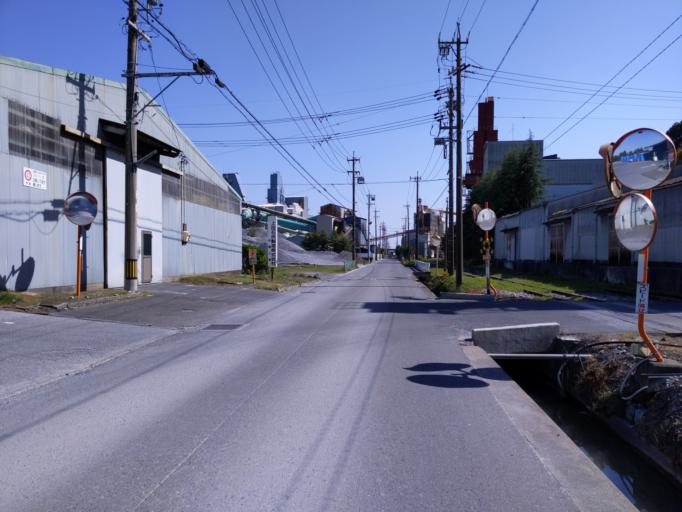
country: JP
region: Gifu
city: Godo
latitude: 35.4013
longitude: 136.5805
